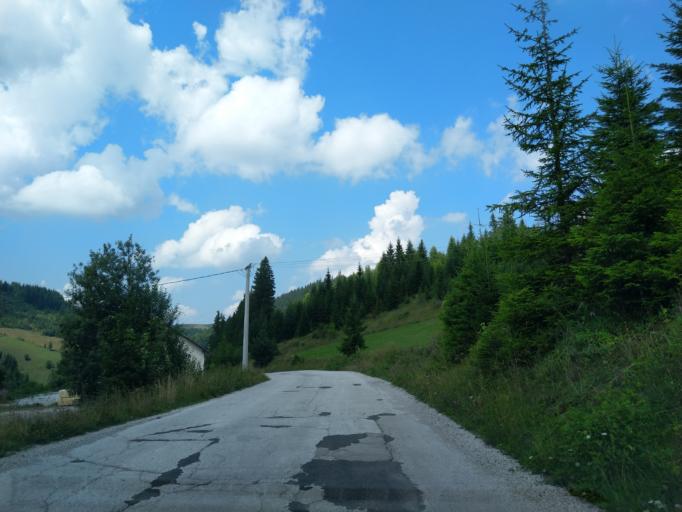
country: RS
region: Central Serbia
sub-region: Zlatiborski Okrug
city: Nova Varos
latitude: 43.5413
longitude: 19.9017
